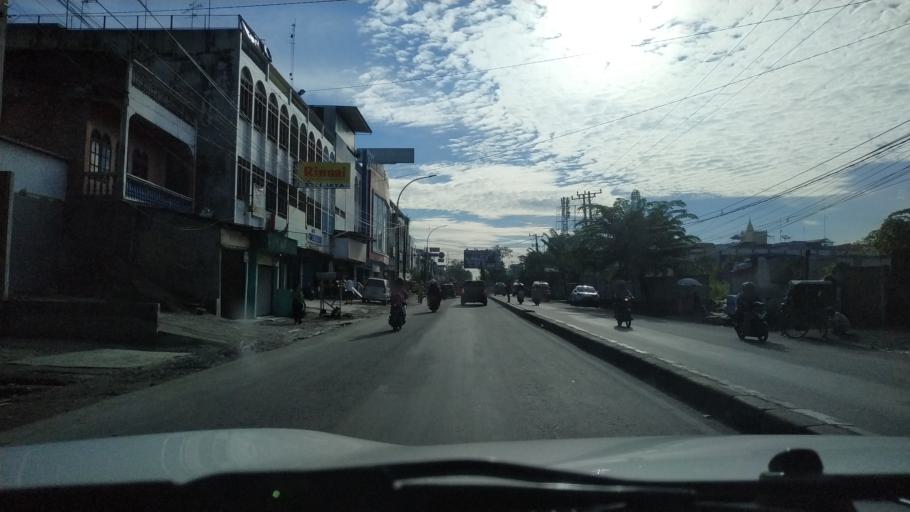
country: ID
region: North Sumatra
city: Medan
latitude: 3.5980
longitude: 98.7051
